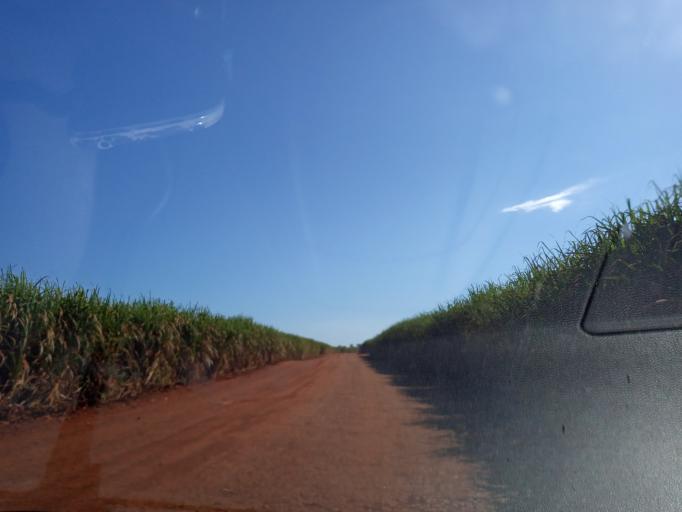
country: BR
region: Goias
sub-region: Itumbiara
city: Itumbiara
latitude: -18.4492
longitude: -49.1786
